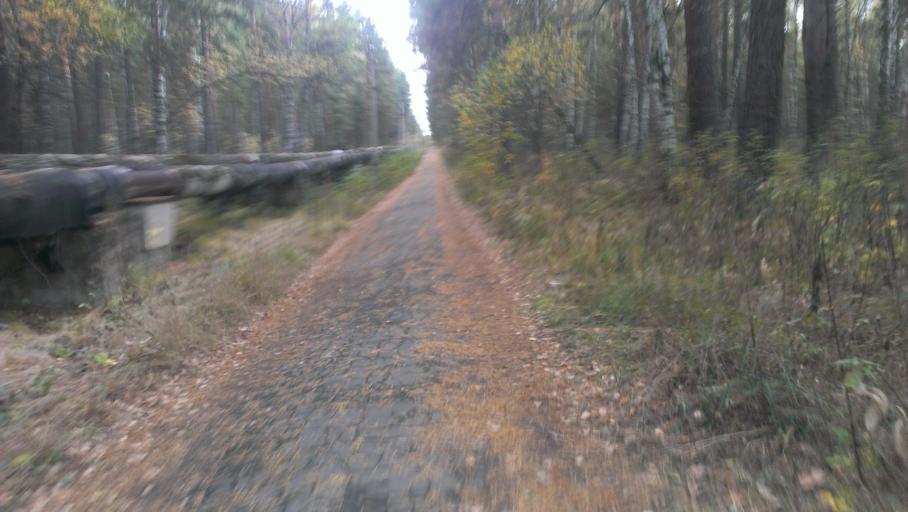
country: RU
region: Altai Krai
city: Yuzhnyy
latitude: 53.2683
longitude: 83.6824
